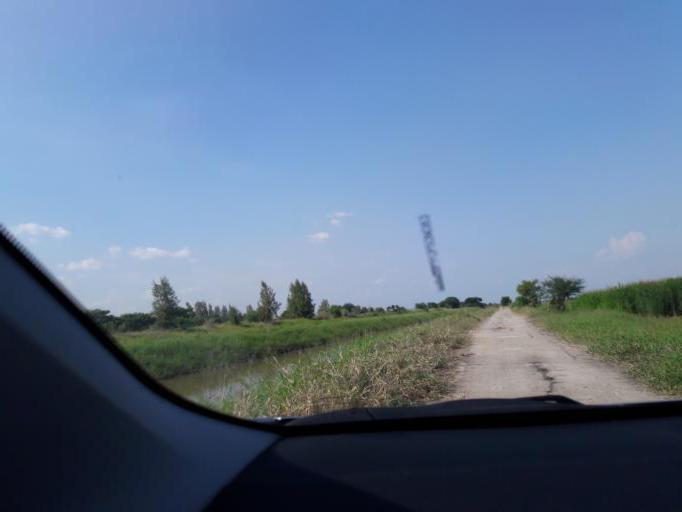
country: TH
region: Ang Thong
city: Ang Thong
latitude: 14.5500
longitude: 100.4067
